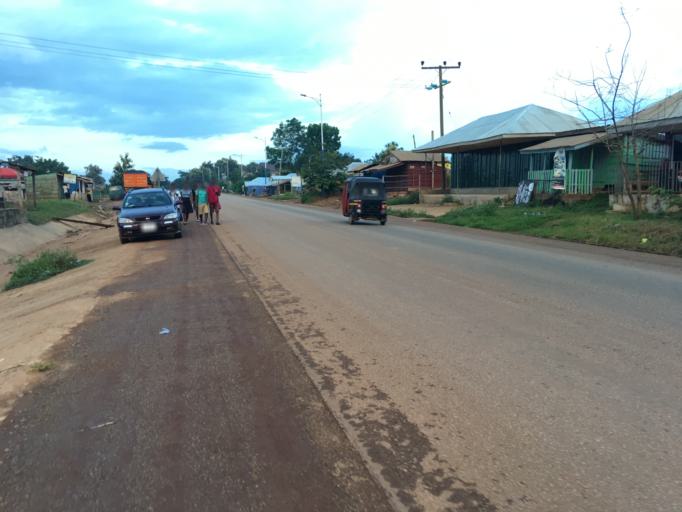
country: GH
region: Western
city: Bibiani
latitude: 6.7898
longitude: -2.5167
